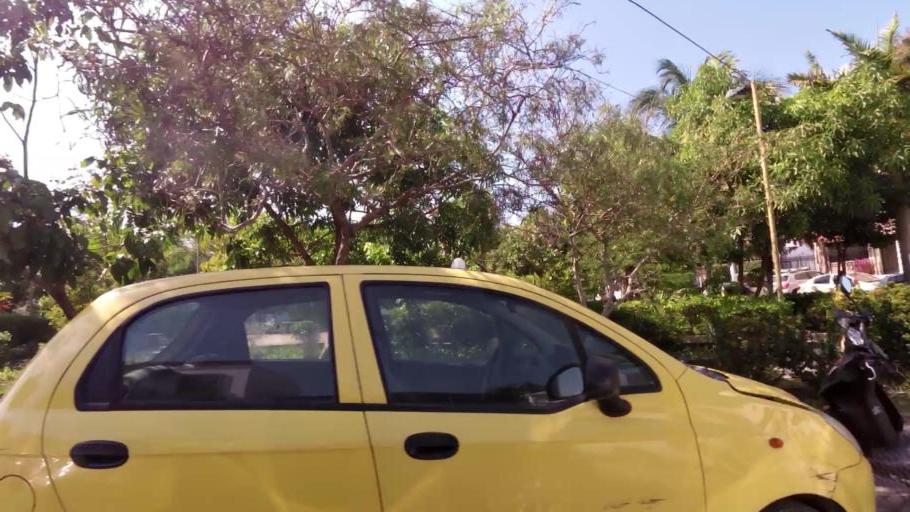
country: CO
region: Bolivar
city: Cartagena
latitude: 10.3859
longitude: -75.4728
